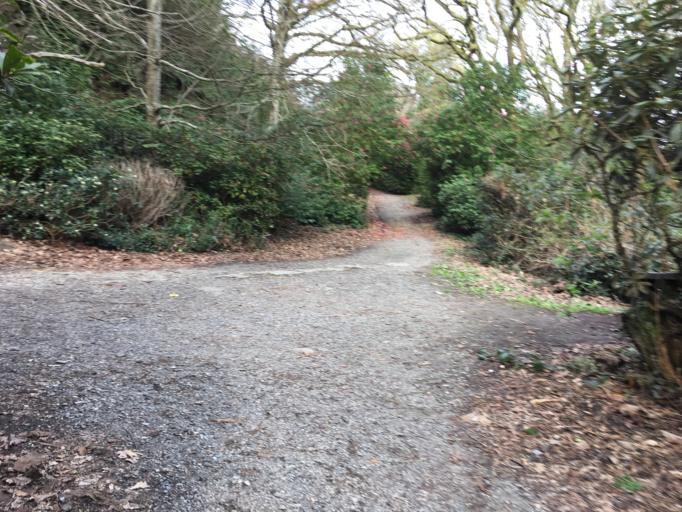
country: GB
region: Wales
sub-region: Gwynedd
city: Porthmadog
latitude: 52.9102
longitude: -4.1023
